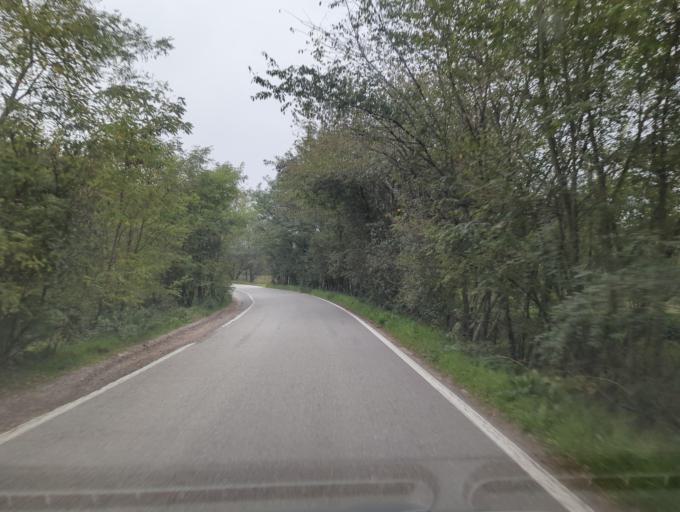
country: IT
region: Lombardy
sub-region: Citta metropolitana di Milano
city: Nosate
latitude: 45.5542
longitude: 8.7372
